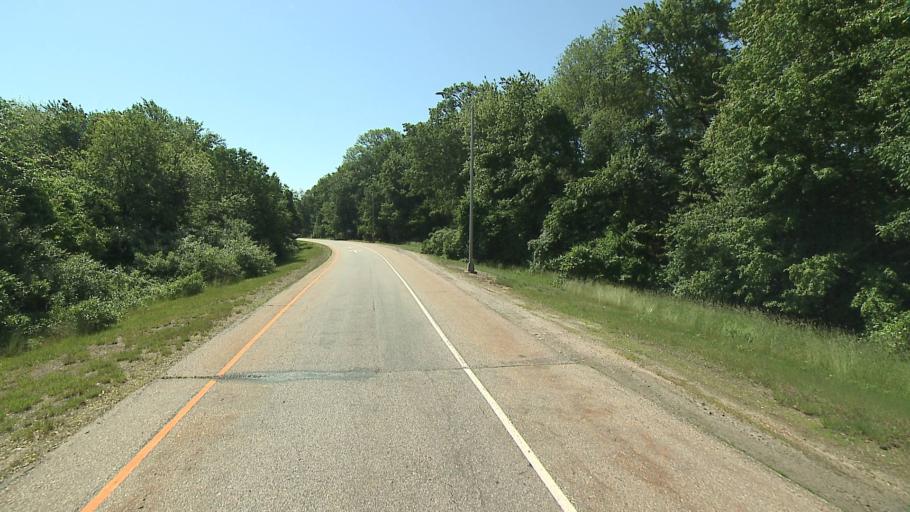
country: US
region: Connecticut
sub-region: New London County
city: Oxoboxo River
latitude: 41.4834
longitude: -72.1022
